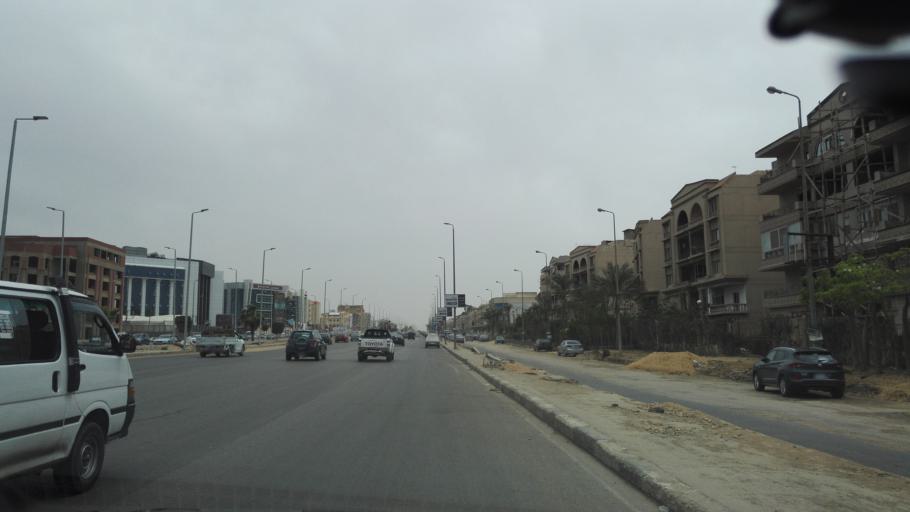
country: EG
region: Muhafazat al Qalyubiyah
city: Al Khankah
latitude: 30.0253
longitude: 31.4778
